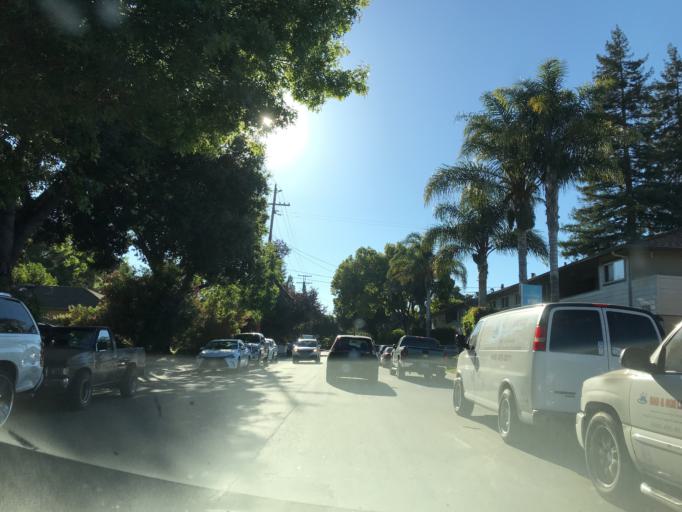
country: US
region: California
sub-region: San Mateo County
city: Menlo Park
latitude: 37.4620
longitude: -122.1620
